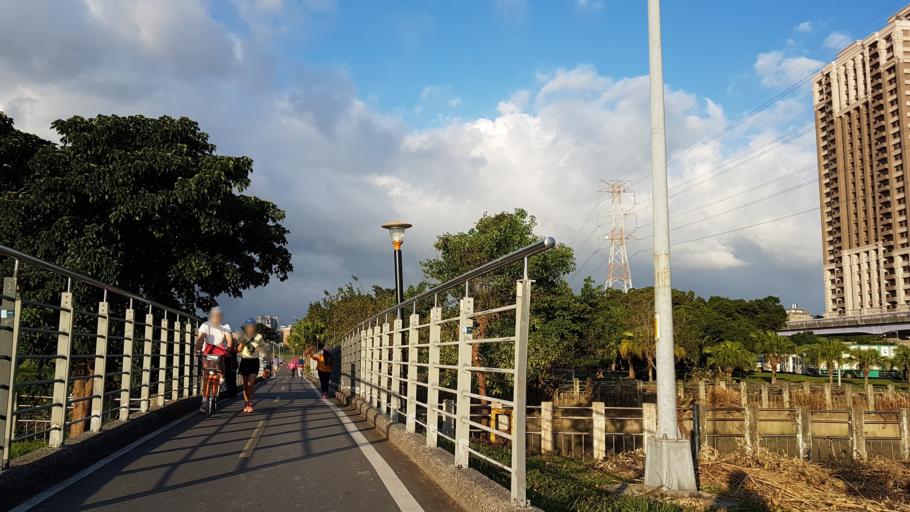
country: TW
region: Taipei
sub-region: Taipei
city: Banqiao
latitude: 25.0136
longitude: 121.5035
